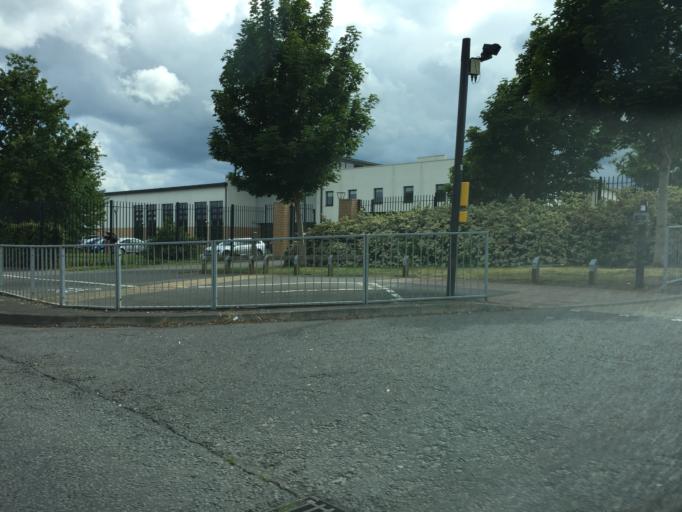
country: GB
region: England
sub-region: Borough of Swindon
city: Swindon
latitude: 51.5654
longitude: -1.7638
